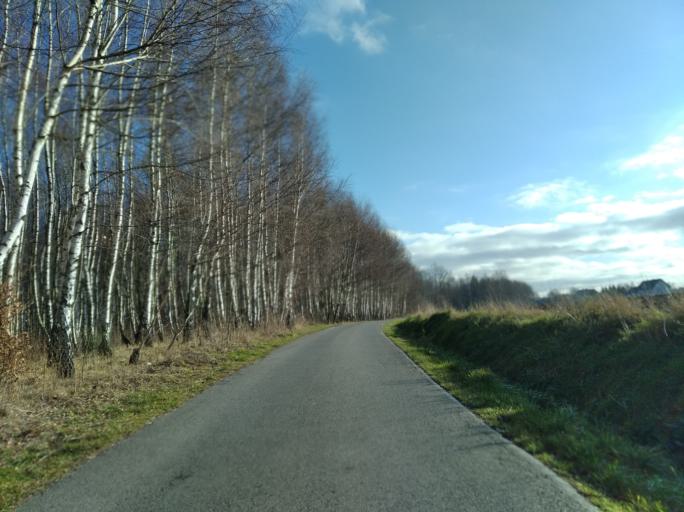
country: PL
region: Subcarpathian Voivodeship
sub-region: Powiat strzyzowski
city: Czudec
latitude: 49.9183
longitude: 21.8403
